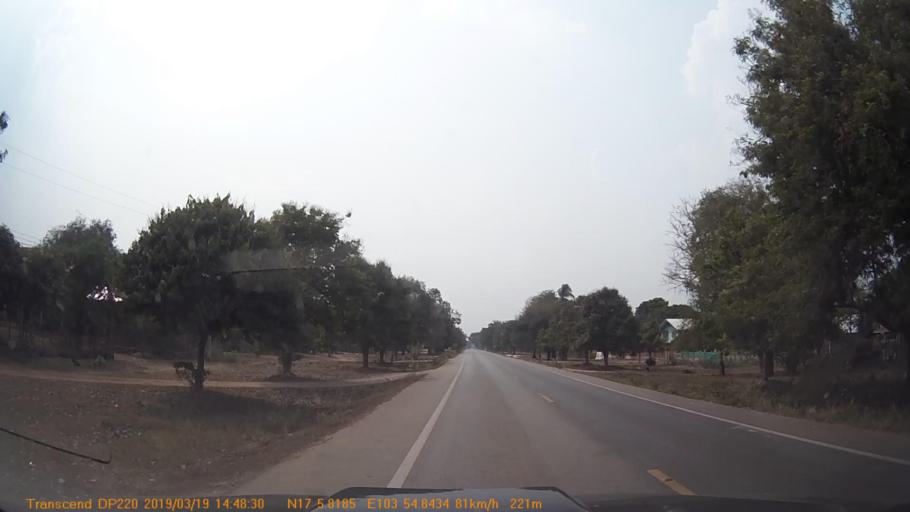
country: TH
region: Sakon Nakhon
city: Kut Bak
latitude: 17.0971
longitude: 103.9138
